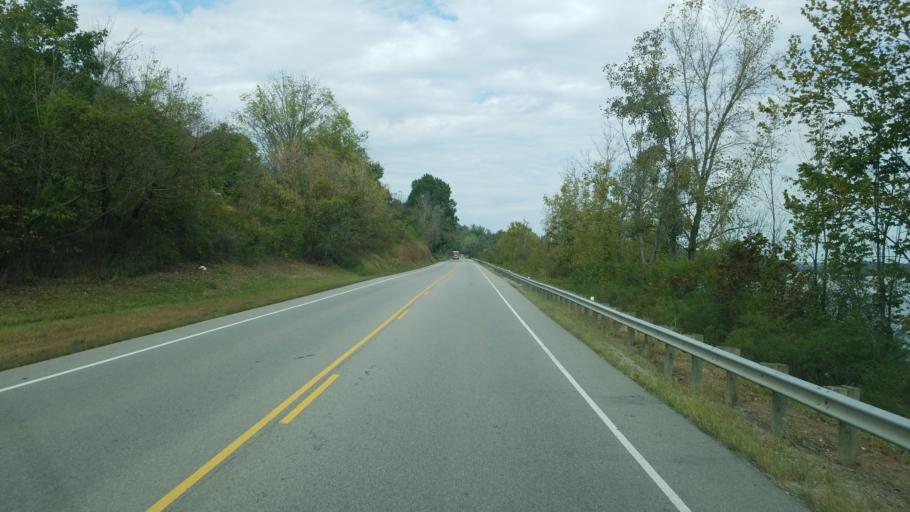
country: US
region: West Virginia
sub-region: Mason County
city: Point Pleasant
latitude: 38.8934
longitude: -82.1453
